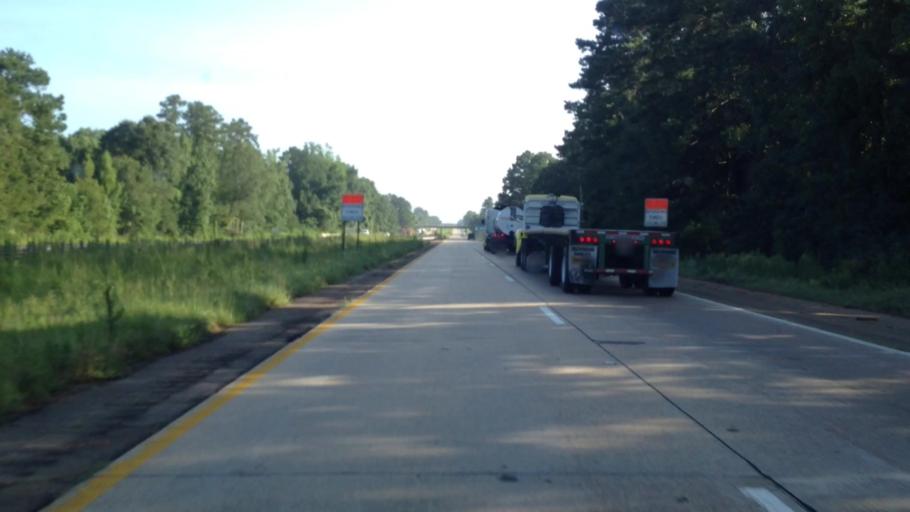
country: US
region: Mississippi
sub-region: Pike County
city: McComb
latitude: 31.2308
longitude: -90.4818
